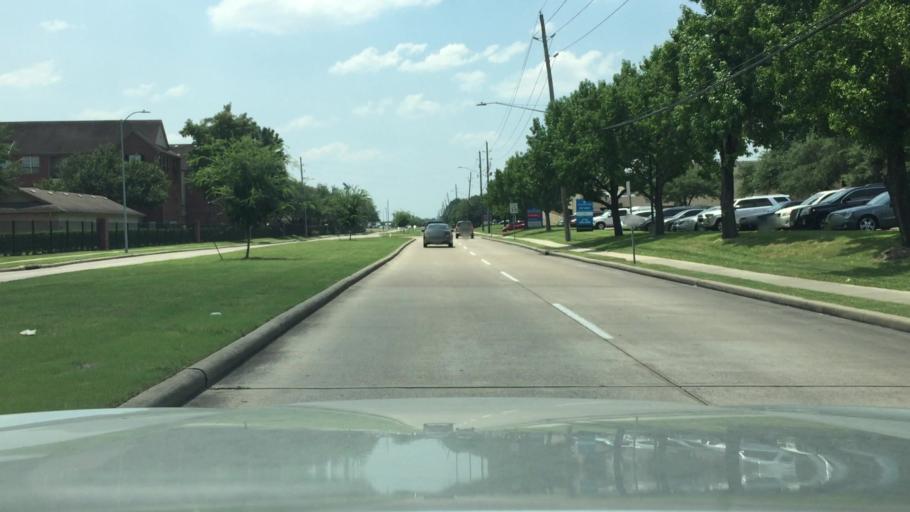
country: US
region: Texas
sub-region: Harris County
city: Bunker Hill Village
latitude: 29.7301
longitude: -95.5925
